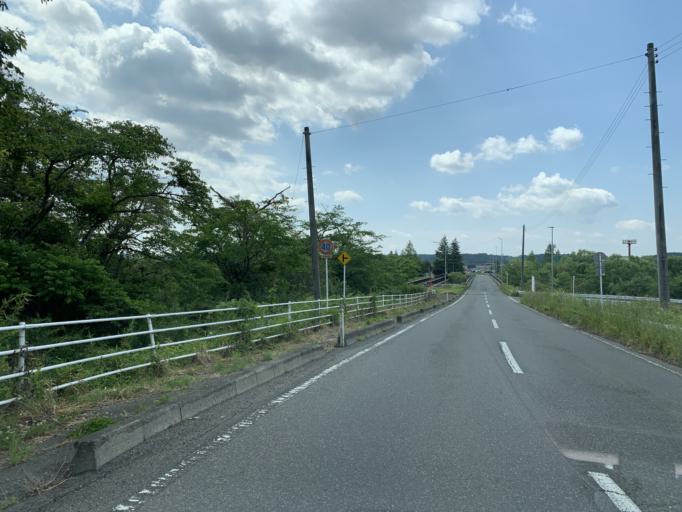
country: JP
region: Miyagi
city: Furukawa
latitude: 38.7477
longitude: 140.9536
